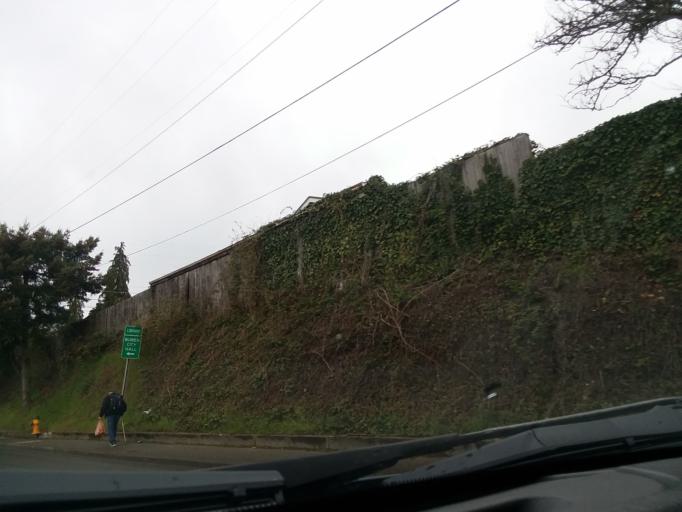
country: US
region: Washington
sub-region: King County
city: Burien
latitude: 47.4705
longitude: -122.3376
